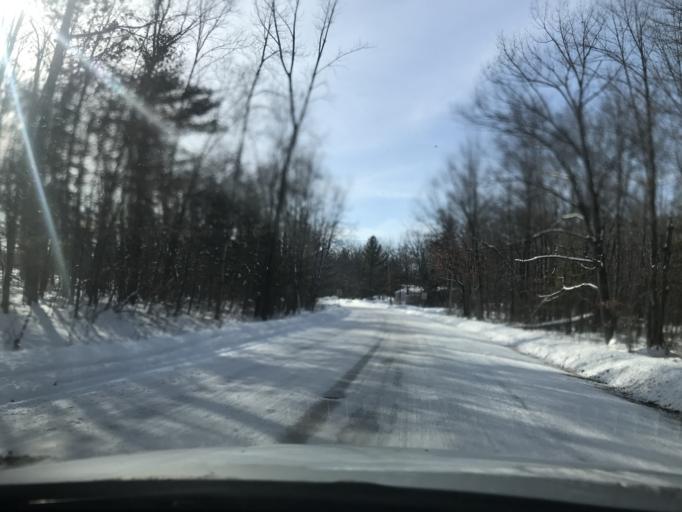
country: US
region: Wisconsin
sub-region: Oconto County
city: Gillett
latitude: 45.1567
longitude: -88.2122
